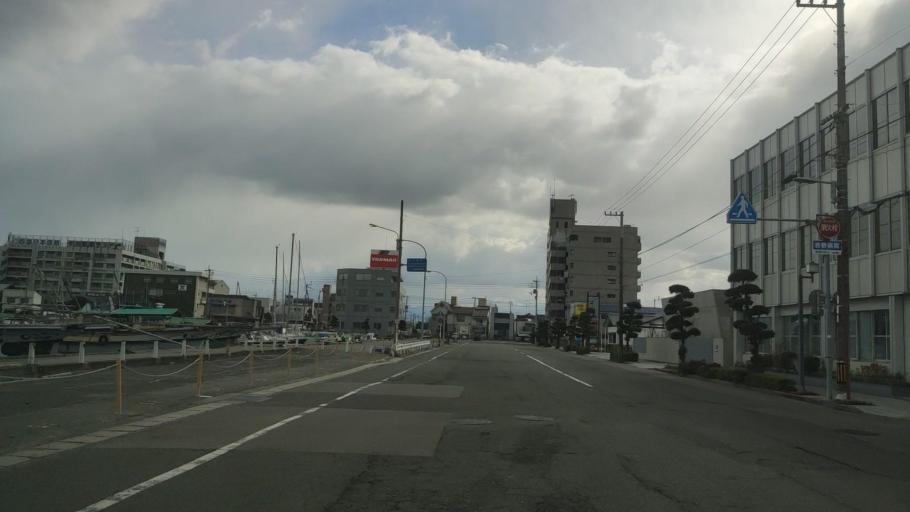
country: JP
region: Ehime
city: Saijo
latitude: 34.0669
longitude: 133.0058
